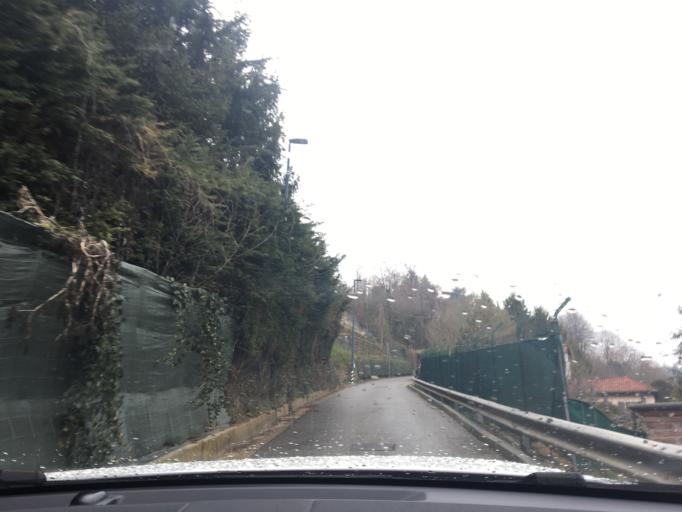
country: IT
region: Piedmont
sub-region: Provincia di Torino
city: Moncalieri
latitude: 45.0217
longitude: 7.6808
